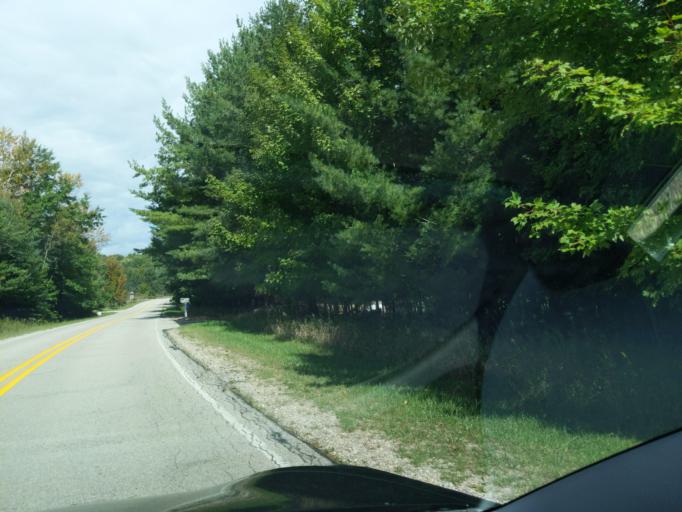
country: US
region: Michigan
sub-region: Antrim County
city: Bellaire
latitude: 44.9743
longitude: -85.3242
